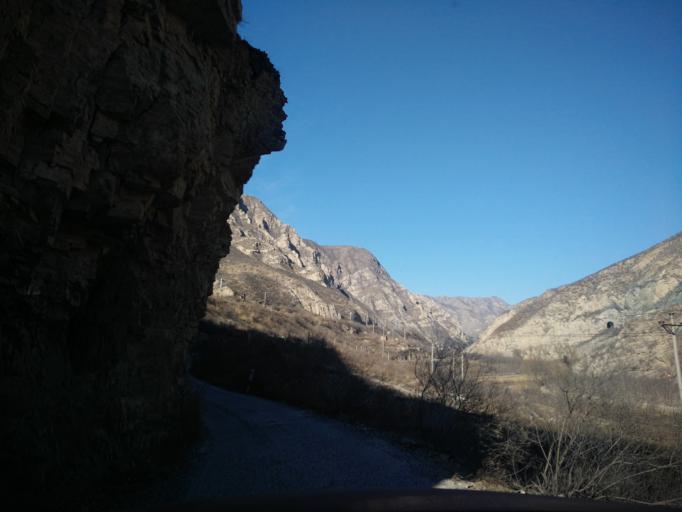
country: CN
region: Beijing
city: Yanjiatai
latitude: 40.1658
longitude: 115.6442
